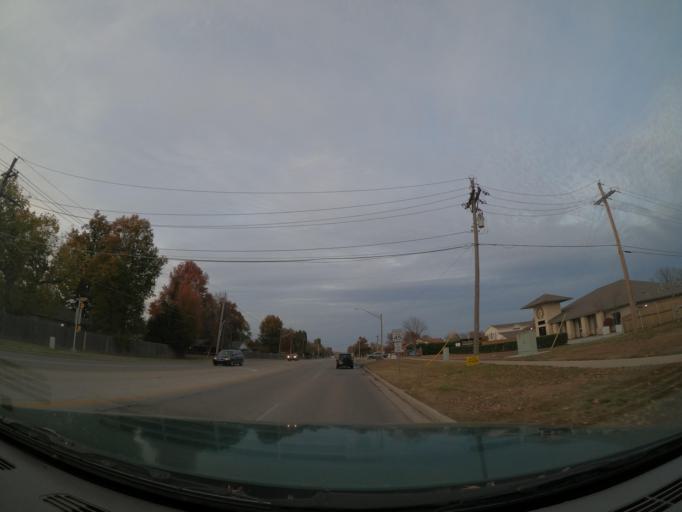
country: US
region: Oklahoma
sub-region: Tulsa County
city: Broken Arrow
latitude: 36.0246
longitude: -95.7974
